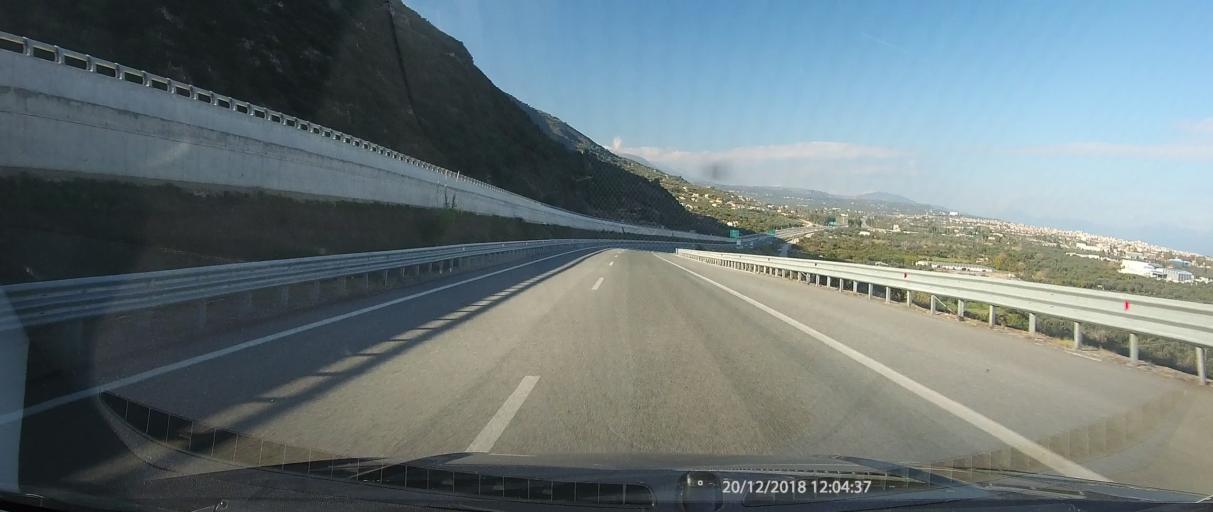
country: GR
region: West Greece
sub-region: Nomos Achaias
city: Temeni
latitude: 38.2140
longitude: 22.1196
